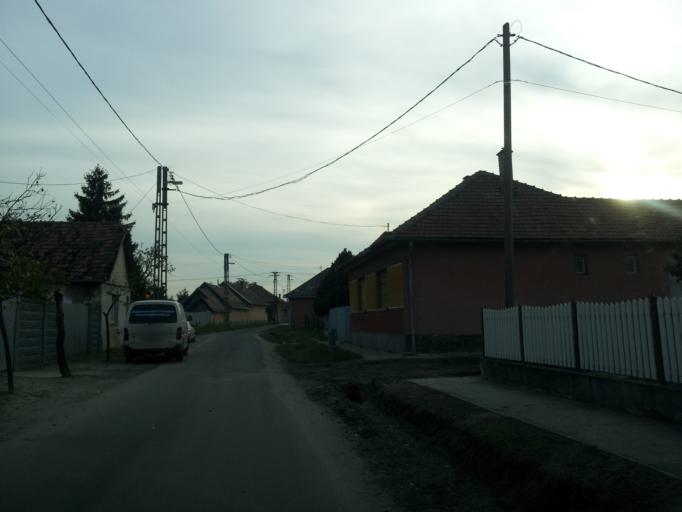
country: HU
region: Pest
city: Nagykata
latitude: 47.4125
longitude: 19.7439
